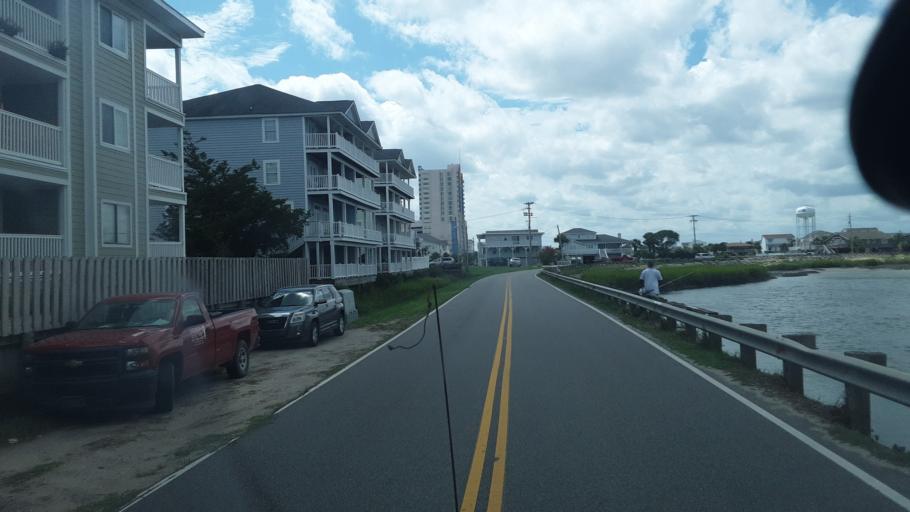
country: US
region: South Carolina
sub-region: Horry County
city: Little River
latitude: 33.8331
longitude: -78.6288
